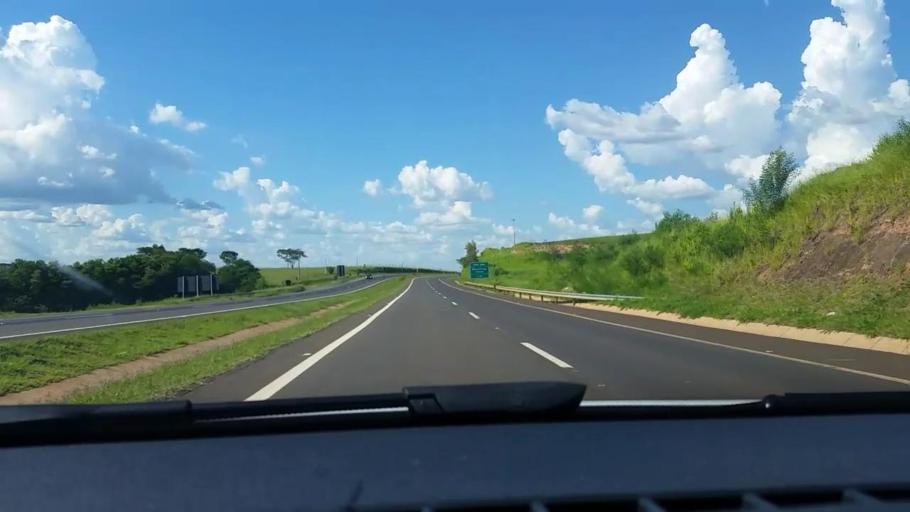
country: BR
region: Sao Paulo
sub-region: Bauru
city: Bauru
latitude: -22.4307
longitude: -49.1323
